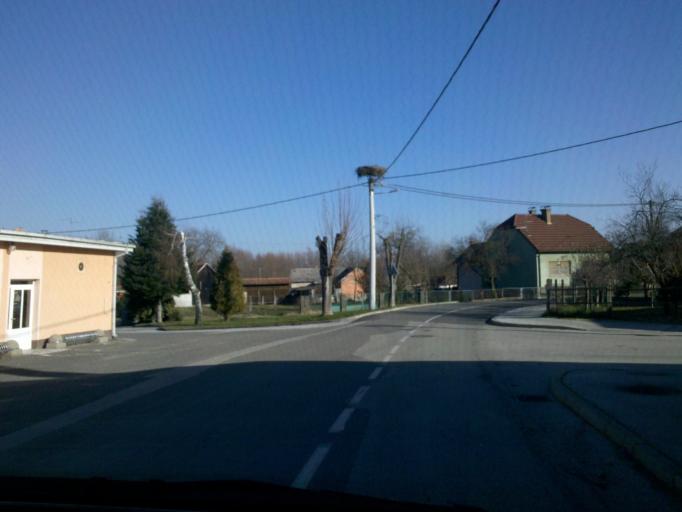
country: HR
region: Medimurska
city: Kotoriba
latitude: 46.3597
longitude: 16.8245
